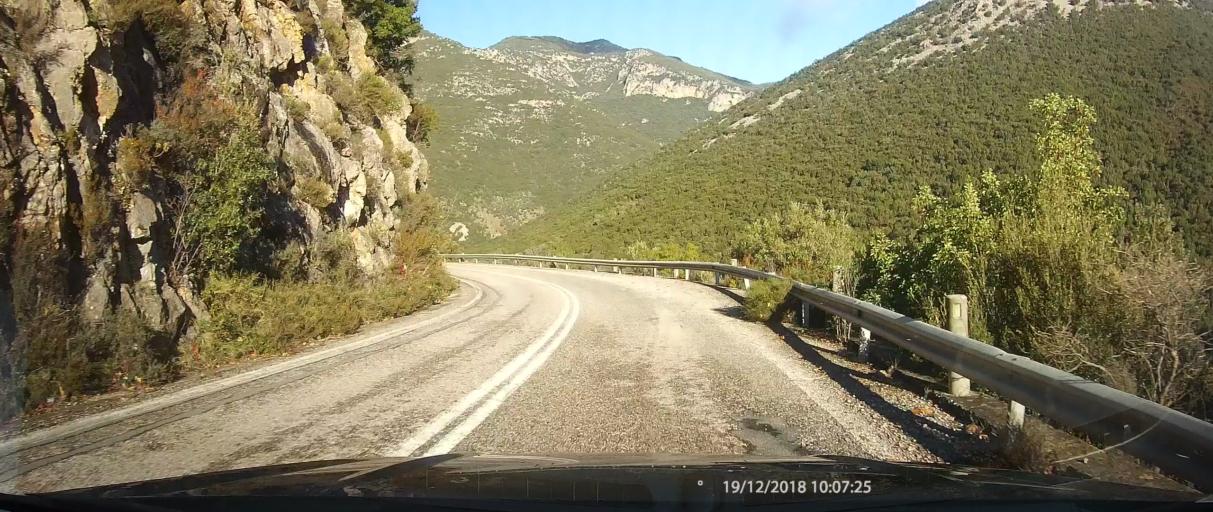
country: GR
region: Peloponnese
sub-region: Nomos Messinias
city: Paralia Vergas
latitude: 37.1115
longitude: 22.2136
